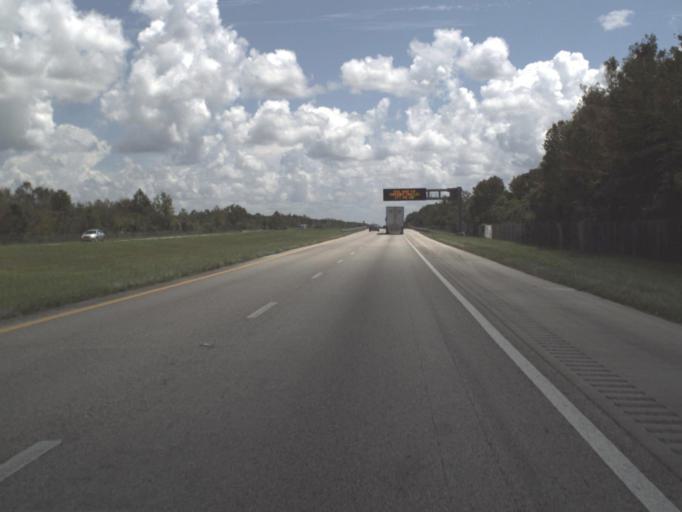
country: US
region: Florida
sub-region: Collier County
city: Orangetree
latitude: 26.1537
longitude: -81.4011
